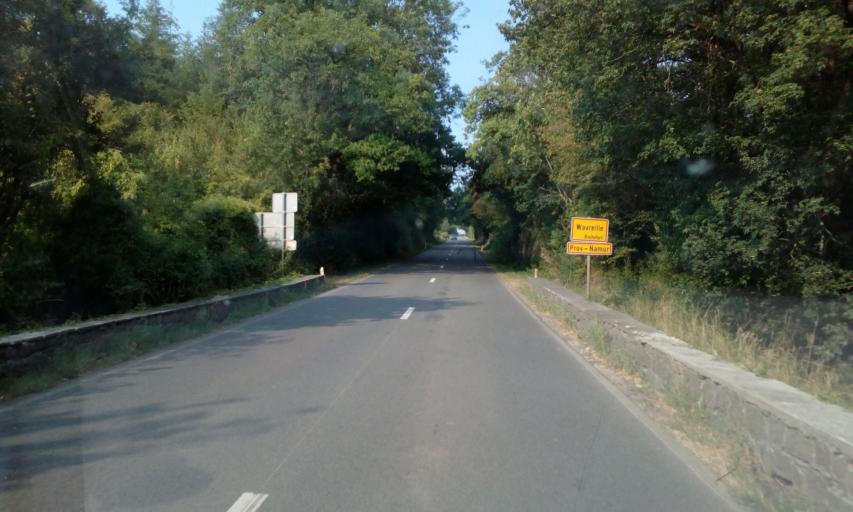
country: BE
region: Wallonia
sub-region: Province du Luxembourg
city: Tellin
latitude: 50.1100
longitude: 5.2384
